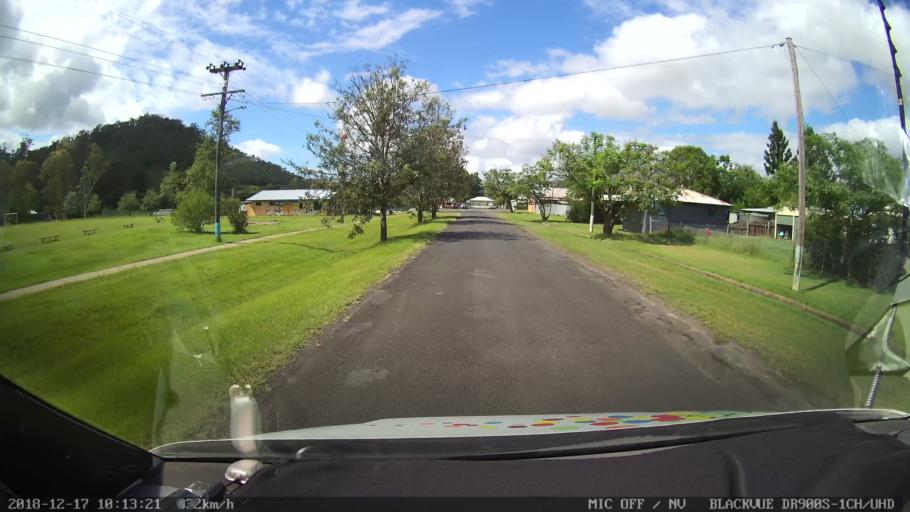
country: AU
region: New South Wales
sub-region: Clarence Valley
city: Gordon
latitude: -28.8898
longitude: 152.5674
